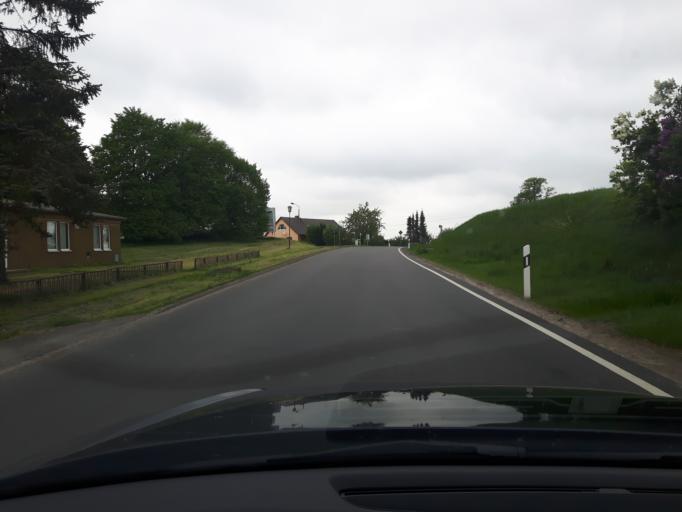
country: DE
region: Mecklenburg-Vorpommern
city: Gnoien
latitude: 54.0167
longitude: 12.6556
